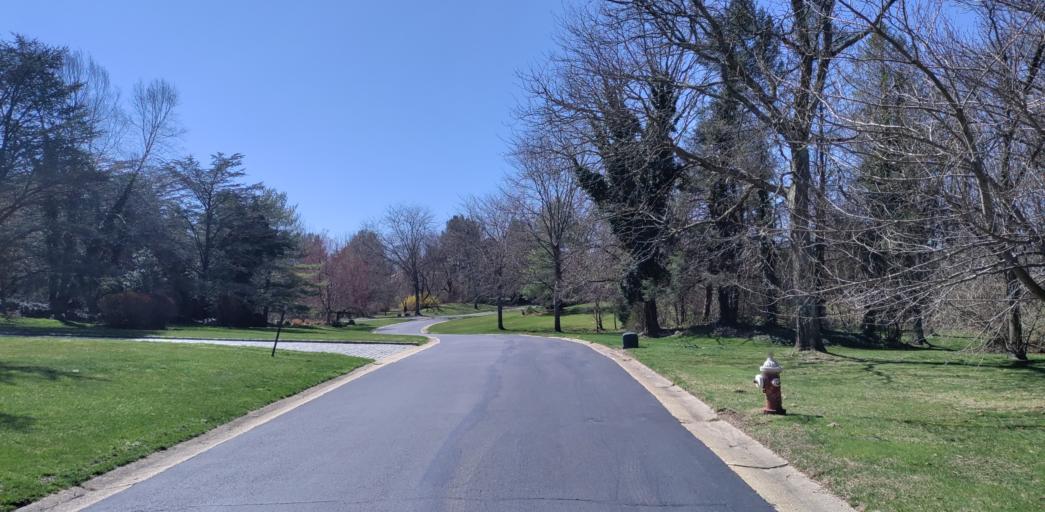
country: US
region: New York
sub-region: Nassau County
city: Old Brookville
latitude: 40.8265
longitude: -73.5955
